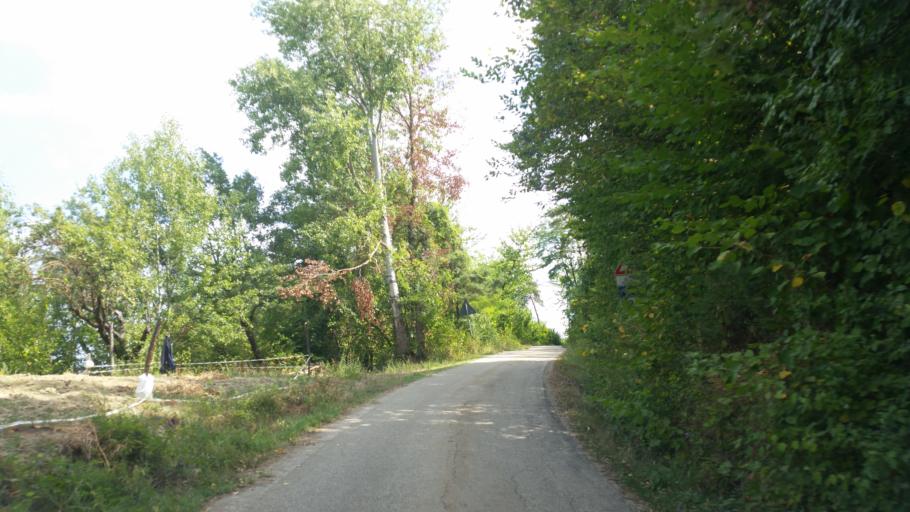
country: IT
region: Piedmont
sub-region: Provincia di Asti
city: Cessole
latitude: 44.6400
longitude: 8.2660
